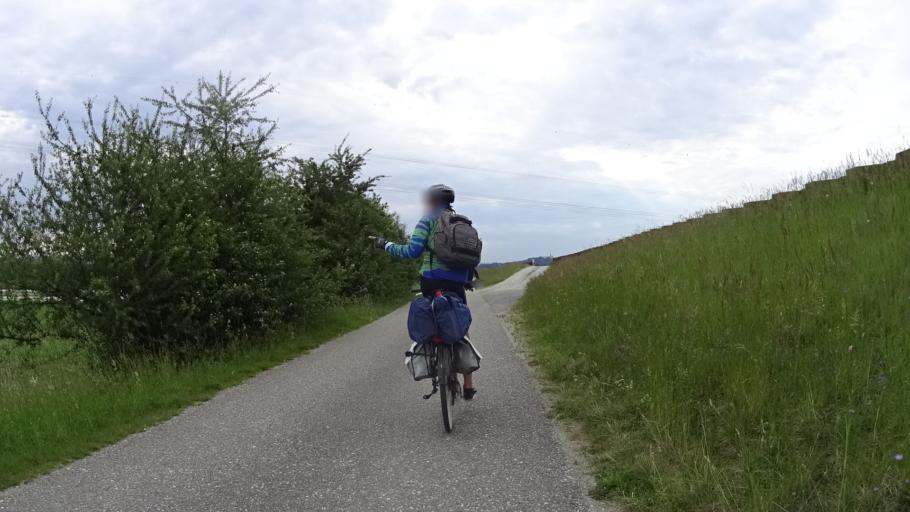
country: DE
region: Bavaria
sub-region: Lower Bavaria
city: Parkstetten
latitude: 48.9093
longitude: 12.6385
